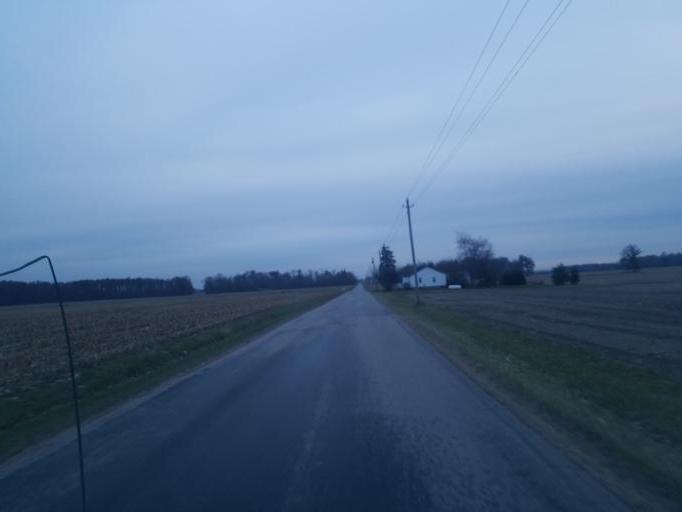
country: US
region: Indiana
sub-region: Adams County
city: Decatur
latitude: 40.7725
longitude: -85.0143
